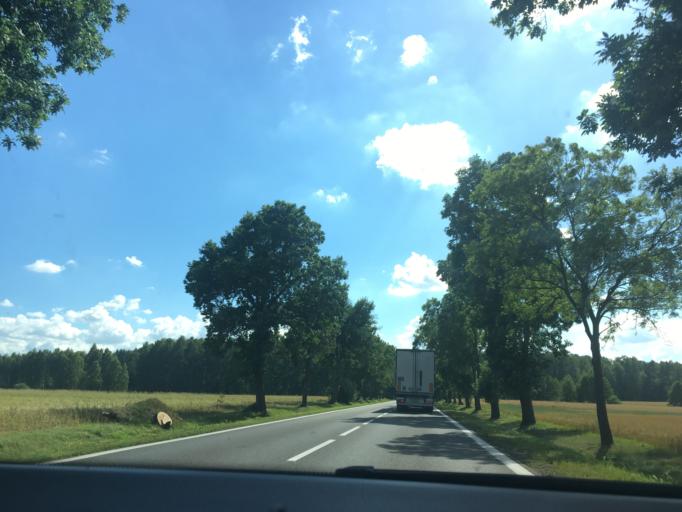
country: PL
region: Podlasie
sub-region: Powiat sokolski
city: Suchowola
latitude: 53.6553
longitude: 23.1258
